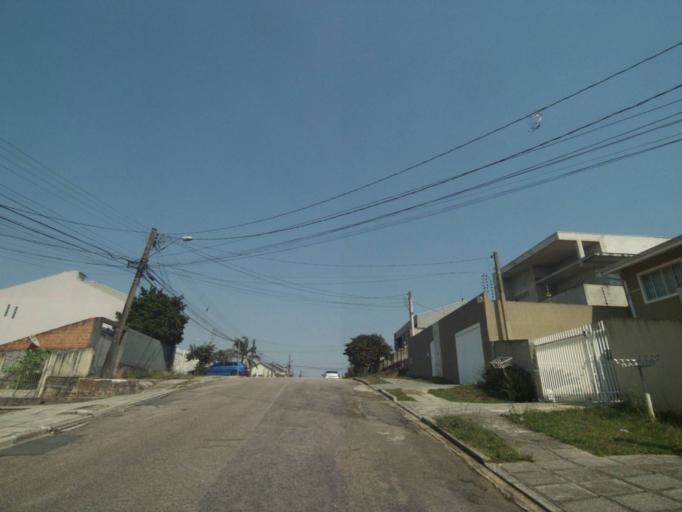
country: BR
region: Parana
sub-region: Sao Jose Dos Pinhais
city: Sao Jose dos Pinhais
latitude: -25.5087
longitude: -49.2714
